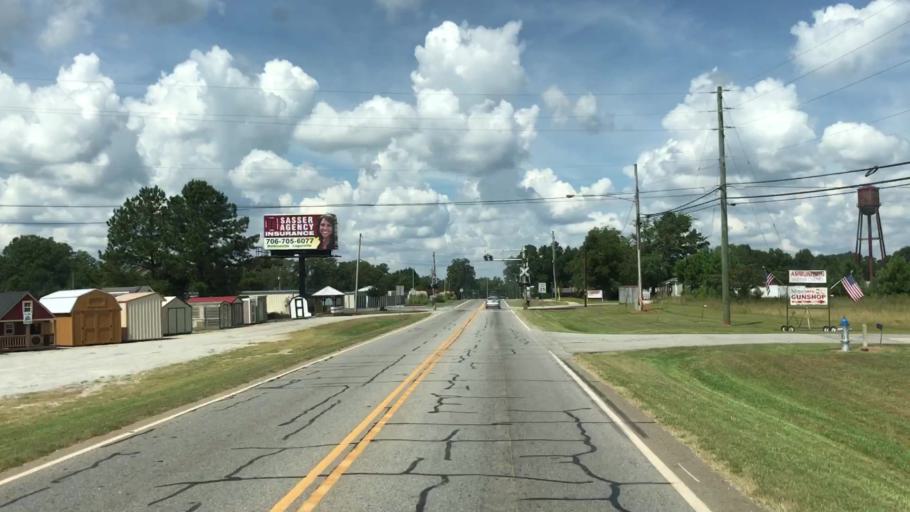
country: US
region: Georgia
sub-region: Oconee County
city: Watkinsville
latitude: 33.8570
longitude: -83.4032
